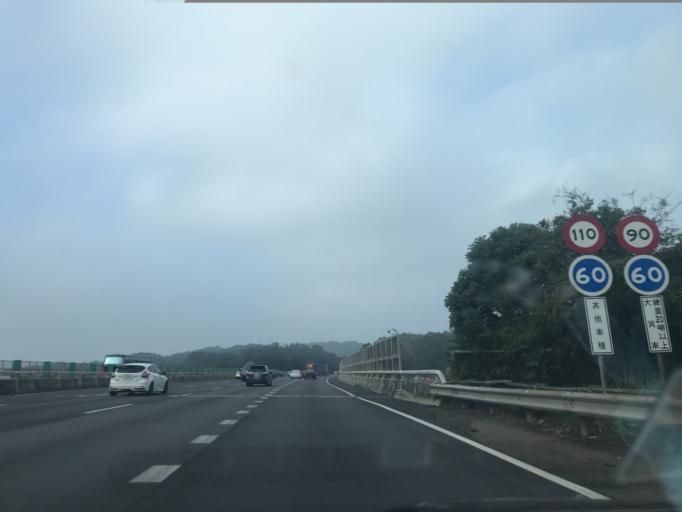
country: TW
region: Taiwan
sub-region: Hsinchu
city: Hsinchu
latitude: 24.7582
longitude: 120.9783
